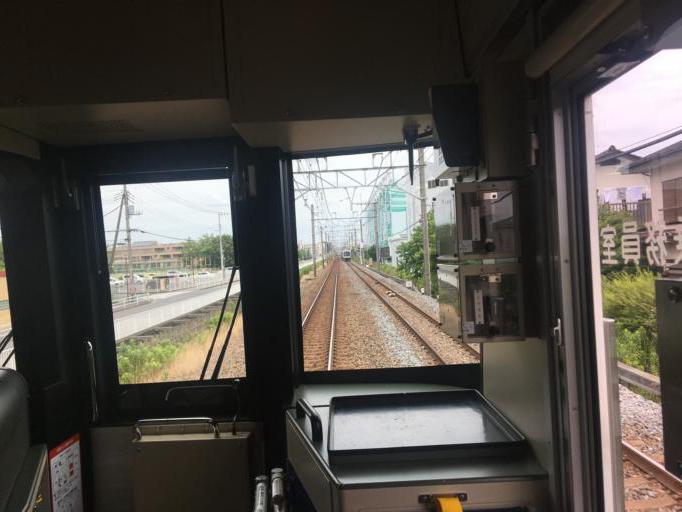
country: JP
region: Saitama
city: Kasukabe
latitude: 35.9412
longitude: 139.7729
